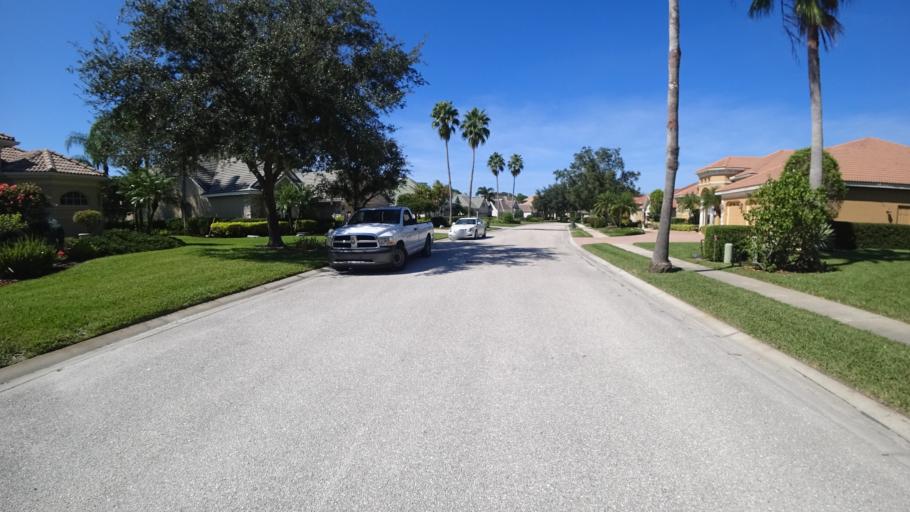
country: US
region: Florida
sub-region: Sarasota County
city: The Meadows
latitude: 27.3941
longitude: -82.4201
